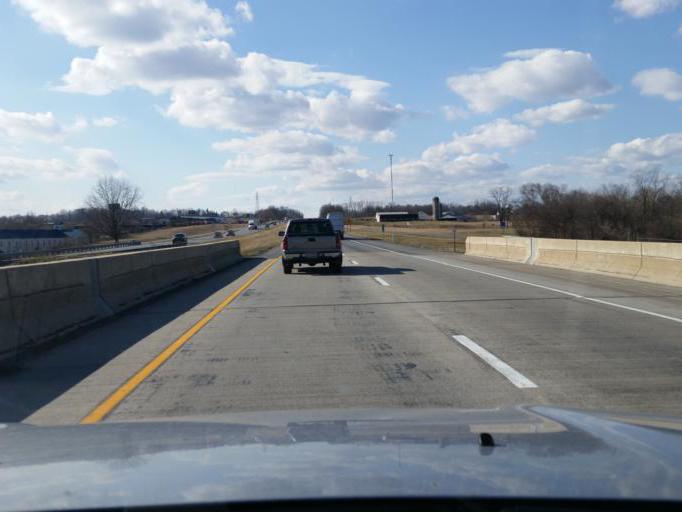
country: US
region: Pennsylvania
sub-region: Lancaster County
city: Rheems
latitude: 40.1437
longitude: -76.5558
